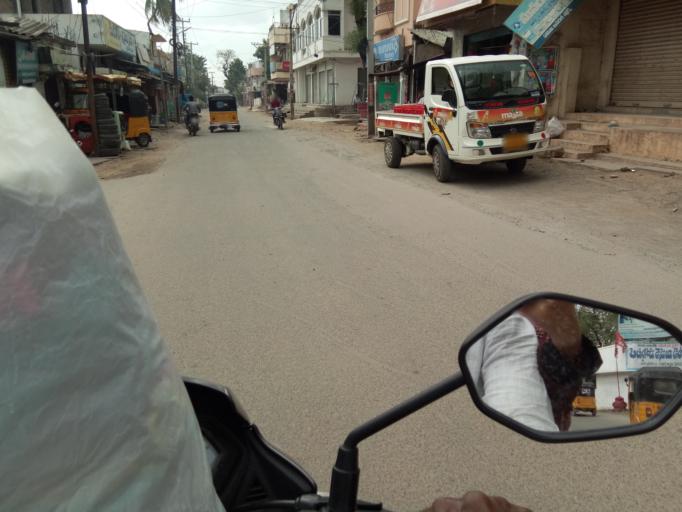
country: IN
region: Telangana
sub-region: Khammam
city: Khammam
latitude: 17.2380
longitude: 80.1456
